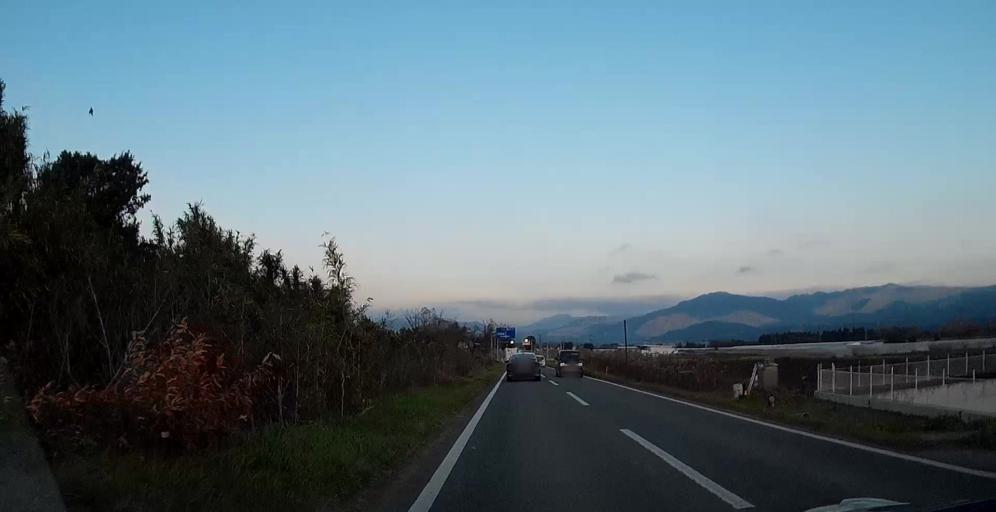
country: JP
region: Kumamoto
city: Ozu
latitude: 32.8310
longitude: 130.8613
